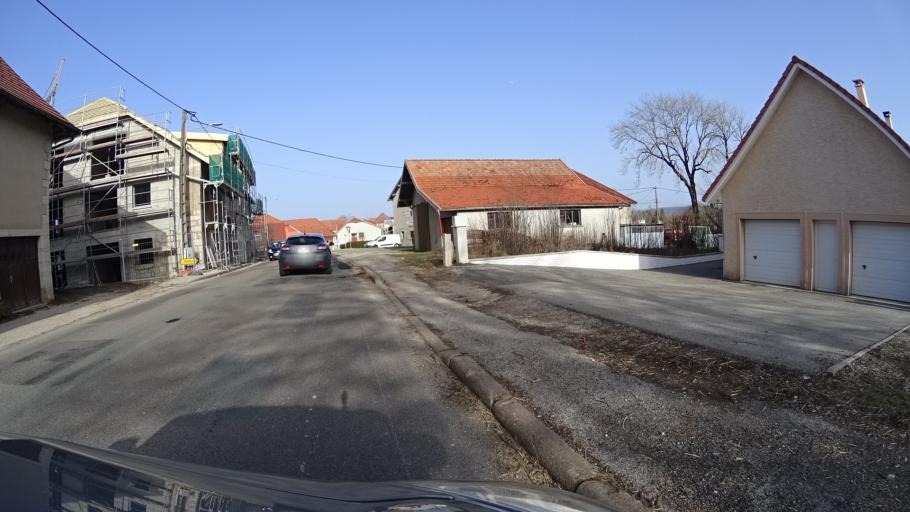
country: FR
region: Franche-Comte
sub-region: Departement du Doubs
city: Frasne
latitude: 46.8709
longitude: 6.1825
